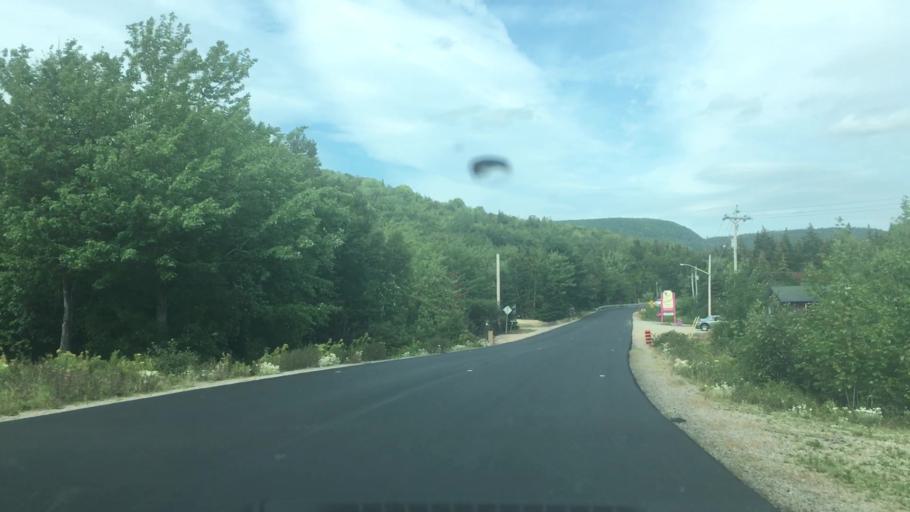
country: CA
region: Nova Scotia
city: Sydney Mines
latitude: 46.5444
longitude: -60.4156
